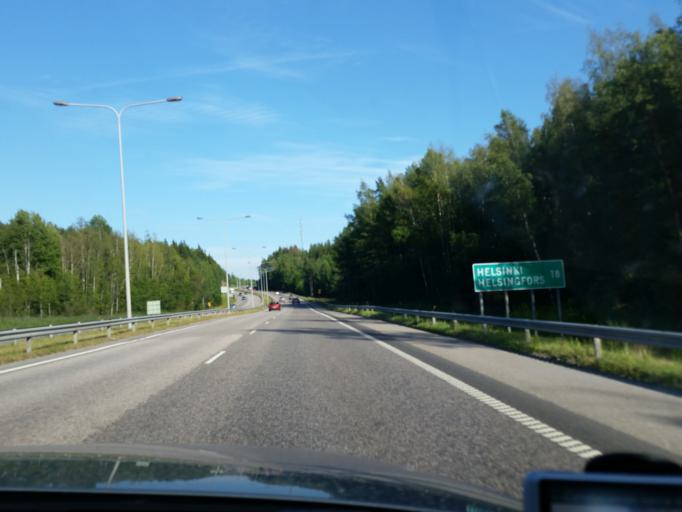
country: FI
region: Uusimaa
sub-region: Helsinki
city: Espoo
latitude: 60.2123
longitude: 24.6728
